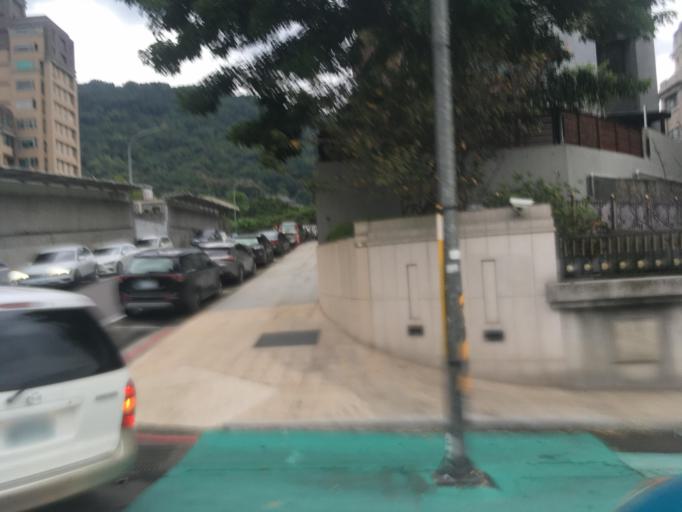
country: TW
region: Taipei
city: Taipei
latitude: 25.1332
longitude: 121.5286
